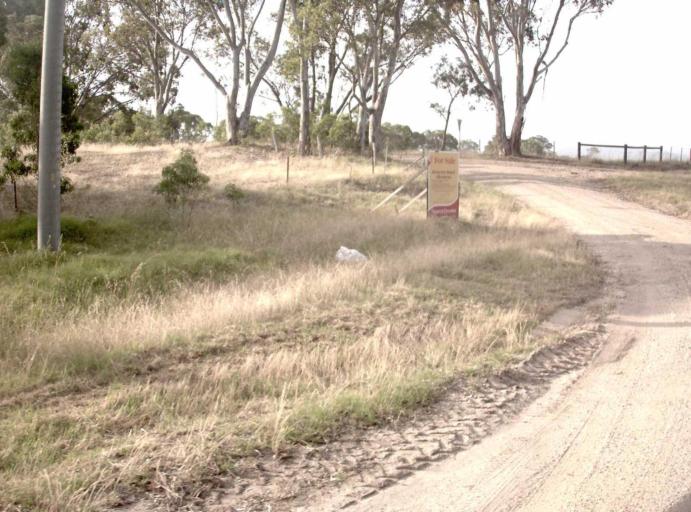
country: AU
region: Victoria
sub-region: Wellington
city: Sale
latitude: -37.9285
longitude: 146.9921
